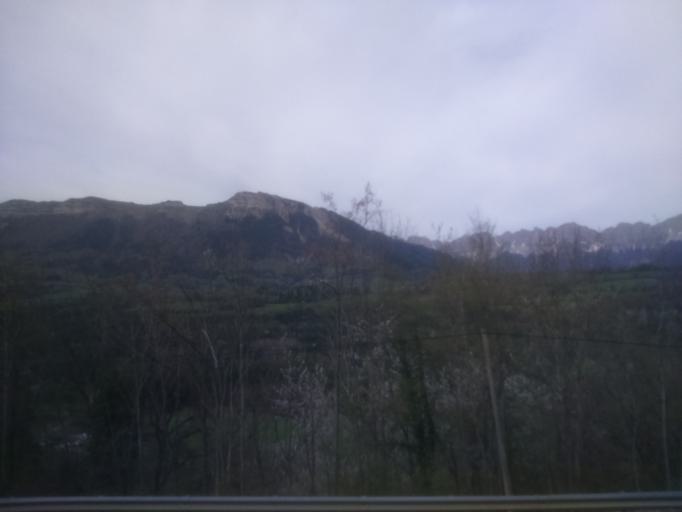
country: FR
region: Rhone-Alpes
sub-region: Departement de l'Isere
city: Le Gua
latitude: 44.9434
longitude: 5.6401
